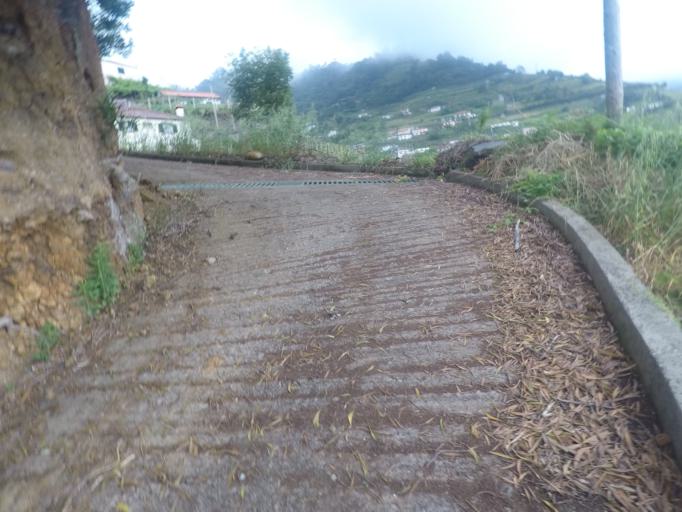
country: PT
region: Madeira
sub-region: Santana
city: Santana
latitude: 32.7697
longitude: -16.8758
